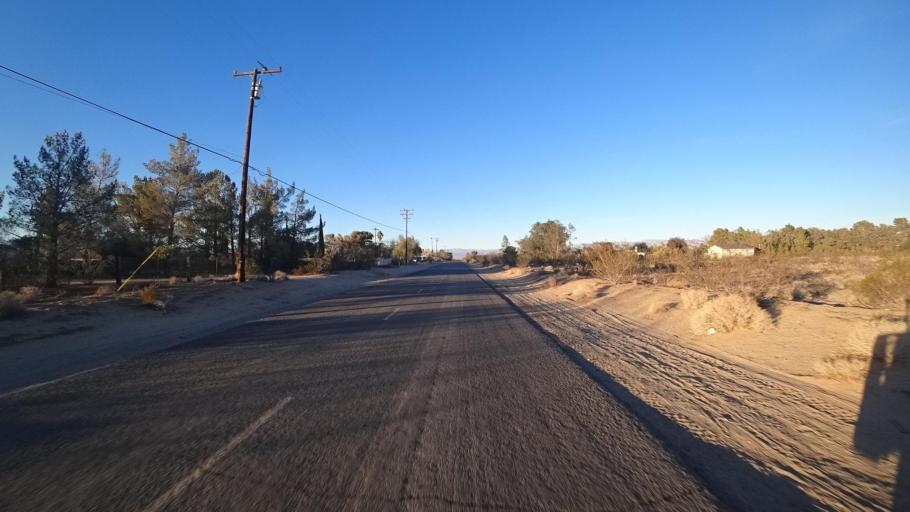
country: US
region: California
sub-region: Kern County
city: Ridgecrest
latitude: 35.6407
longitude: -117.7056
